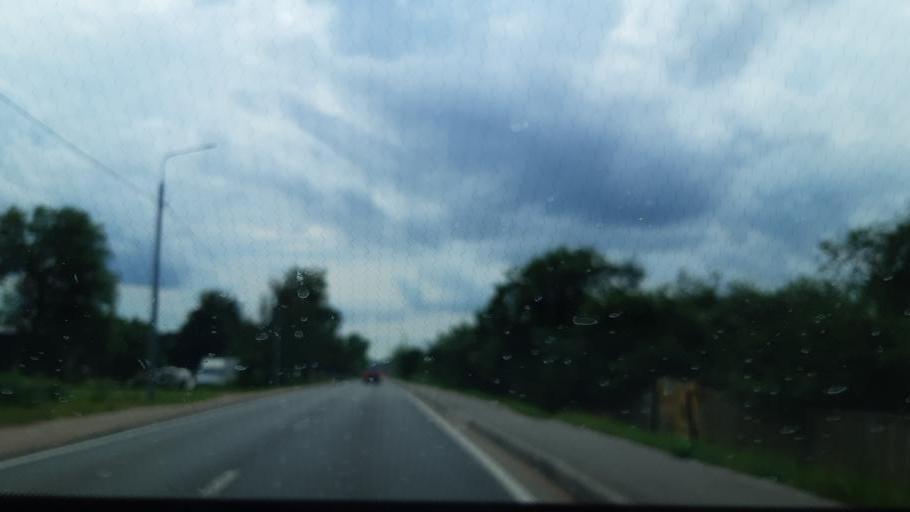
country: RU
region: Moskovskaya
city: Dorokhovo
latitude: 55.5367
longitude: 36.3635
